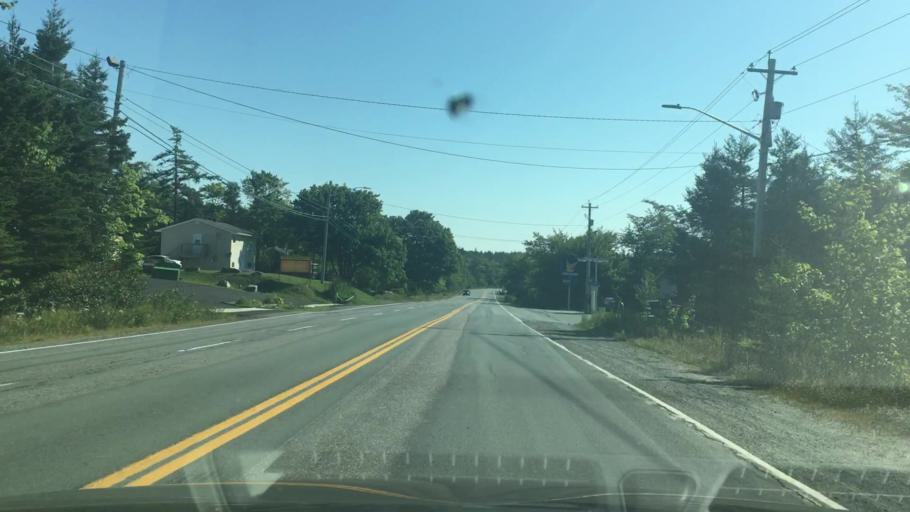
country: CA
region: Nova Scotia
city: Cole Harbour
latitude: 44.7785
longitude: -63.0854
